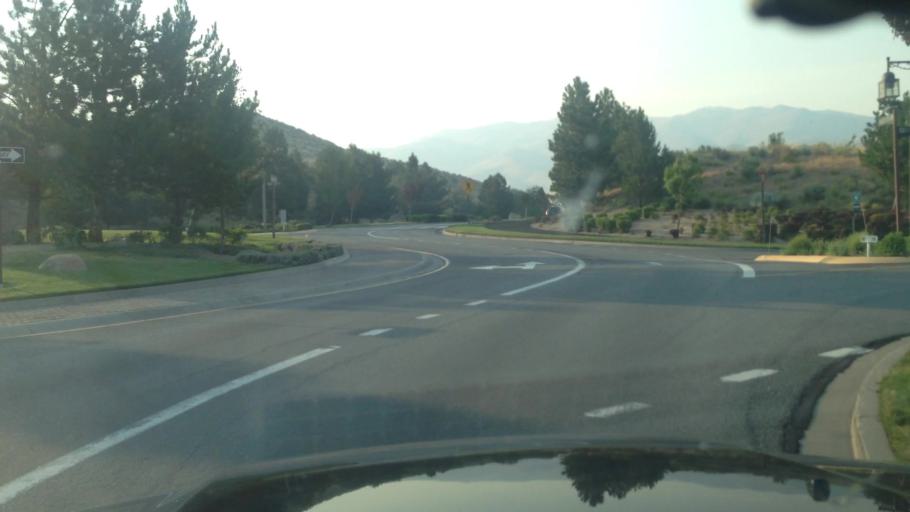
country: US
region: Nevada
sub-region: Washoe County
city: Mogul
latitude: 39.5236
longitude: -119.9107
